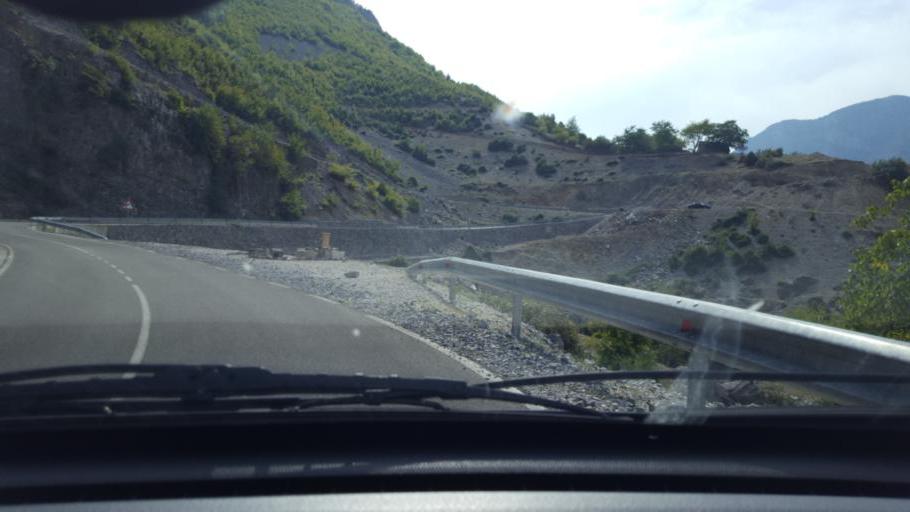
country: AL
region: Shkoder
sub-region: Rrethi i Malesia e Madhe
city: Kastrat
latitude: 42.5062
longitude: 19.6128
